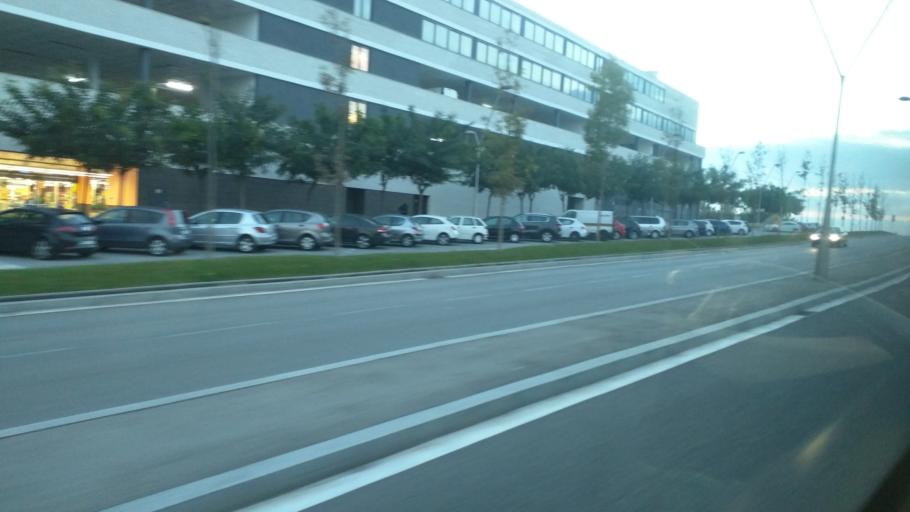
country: ES
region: Catalonia
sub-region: Provincia de Barcelona
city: Sant Feliu de Llobregat
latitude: 41.3765
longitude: 2.0409
